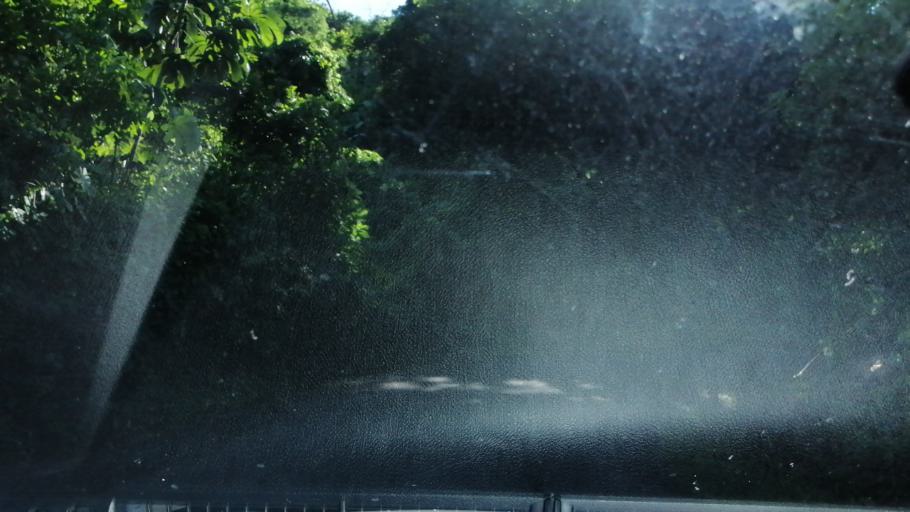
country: SV
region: Morazan
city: Corinto
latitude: 13.7907
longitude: -88.0214
